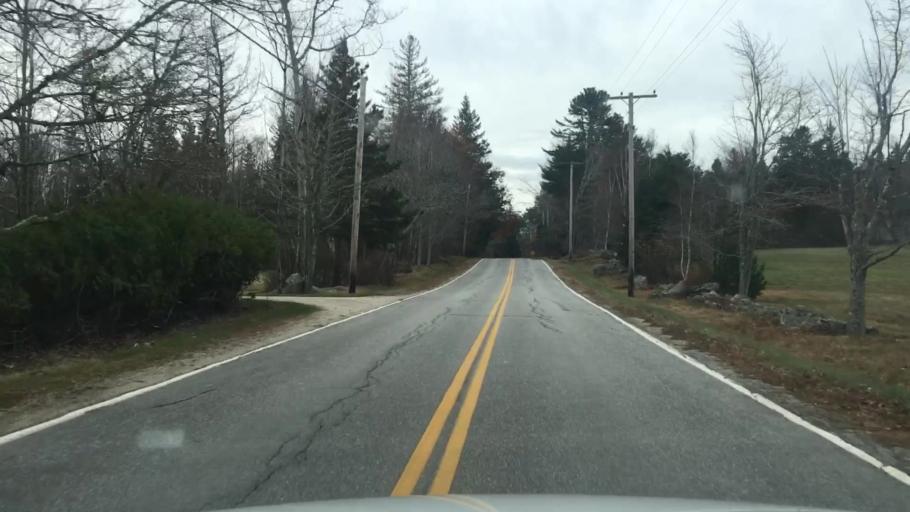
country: US
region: Maine
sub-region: Hancock County
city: Sedgwick
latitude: 44.2938
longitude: -68.5554
